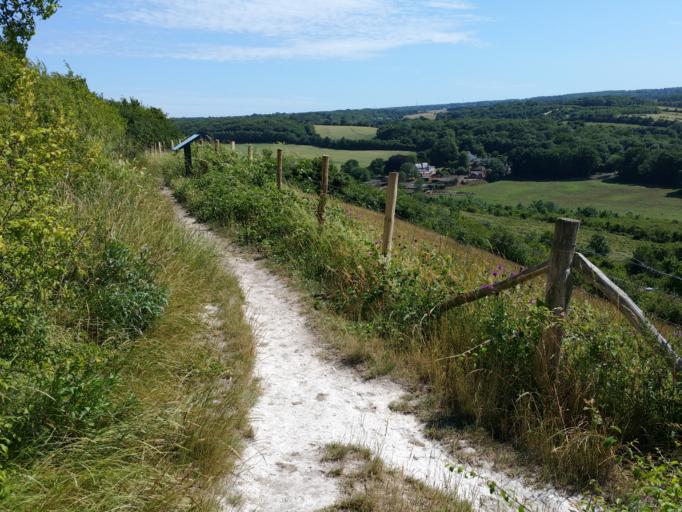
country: GB
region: England
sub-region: Kent
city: Gillingham
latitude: 51.3672
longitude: 0.5581
